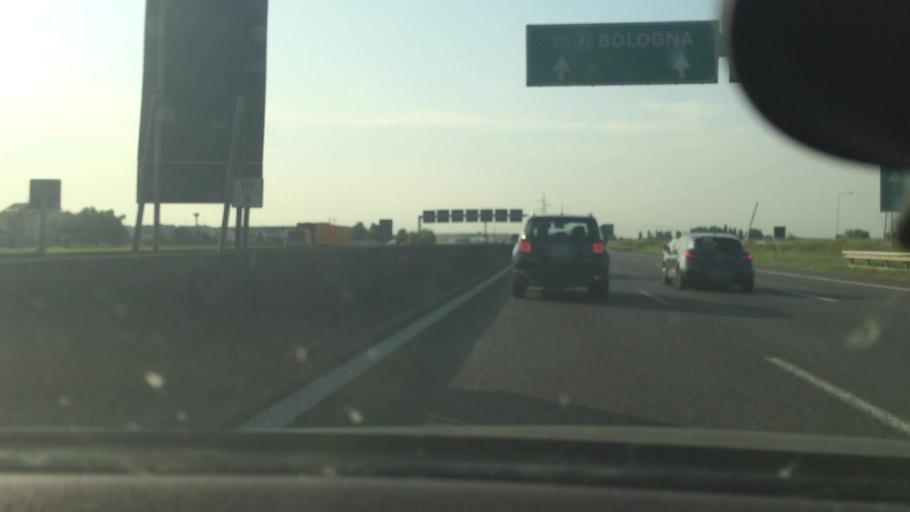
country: IT
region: Lombardy
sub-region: Citta metropolitana di Milano
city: Riozzo
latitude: 45.3465
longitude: 9.3117
